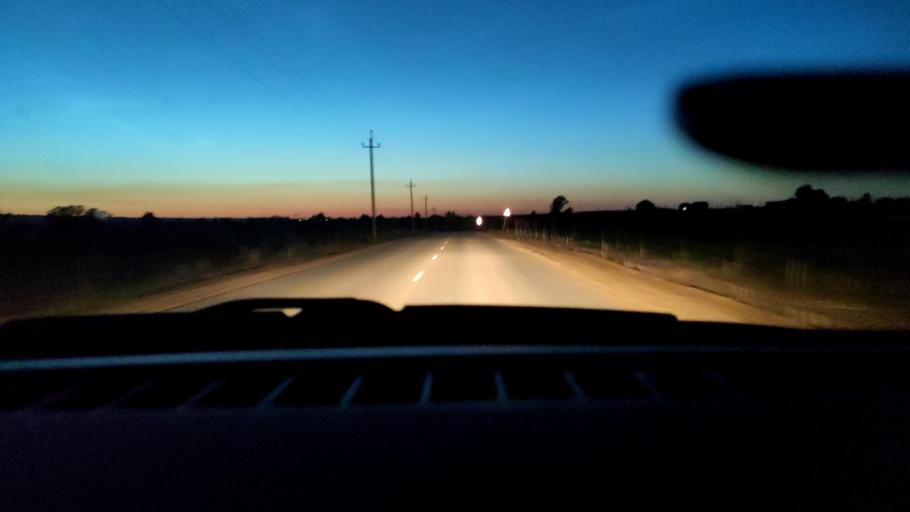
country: RU
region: Perm
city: Kultayevo
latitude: 57.8932
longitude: 55.9911
